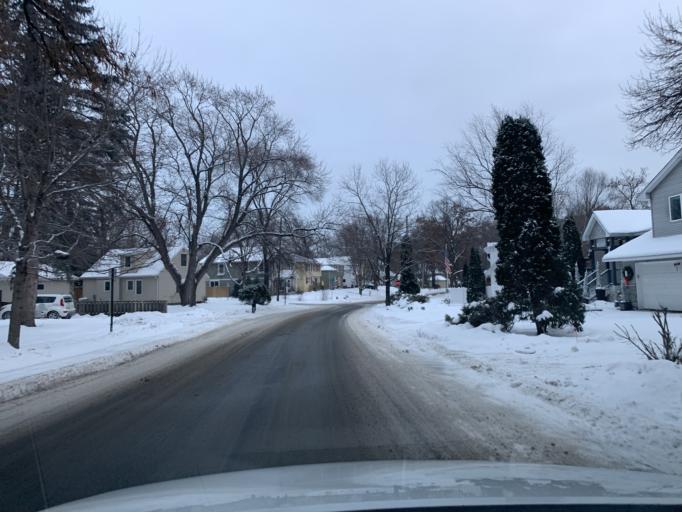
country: US
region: Minnesota
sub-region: Hennepin County
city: Saint Louis Park
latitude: 44.9275
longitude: -93.3418
